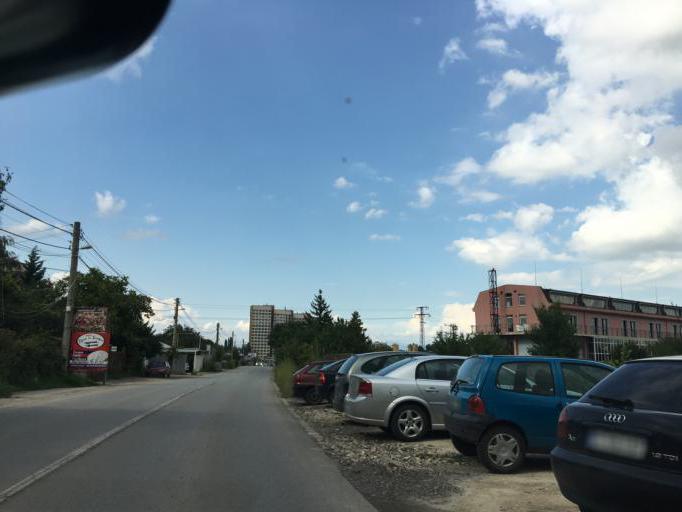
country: BG
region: Sofia-Capital
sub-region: Stolichna Obshtina
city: Sofia
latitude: 42.6422
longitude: 23.3530
